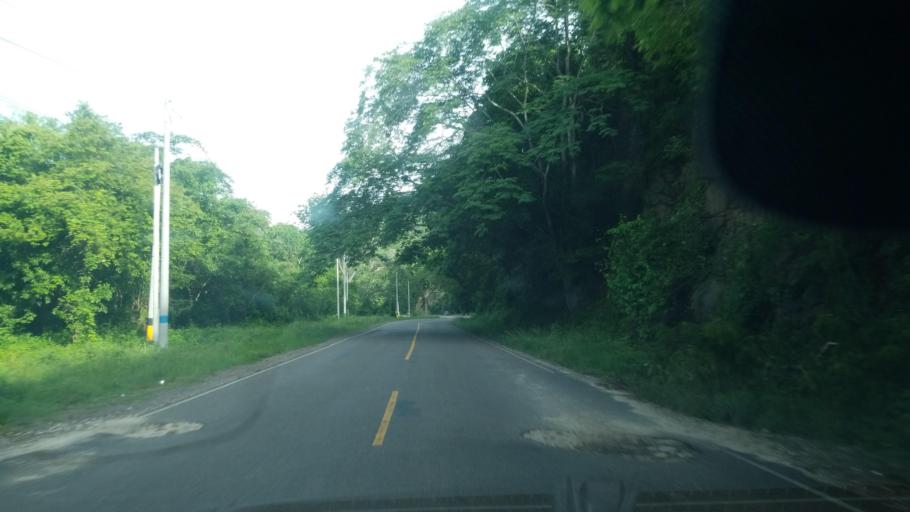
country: HN
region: Santa Barbara
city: Trinidad
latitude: 15.1278
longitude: -88.2101
